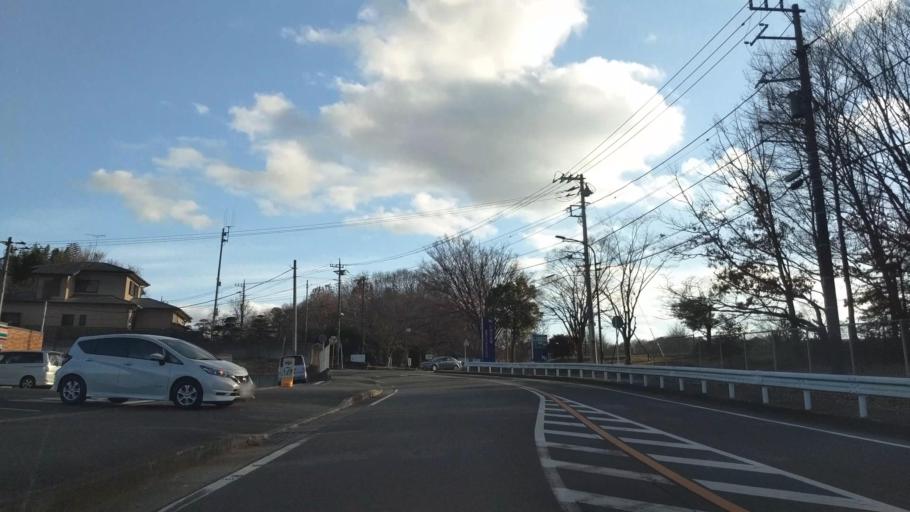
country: JP
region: Kanagawa
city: Hadano
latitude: 35.3490
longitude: 139.2617
